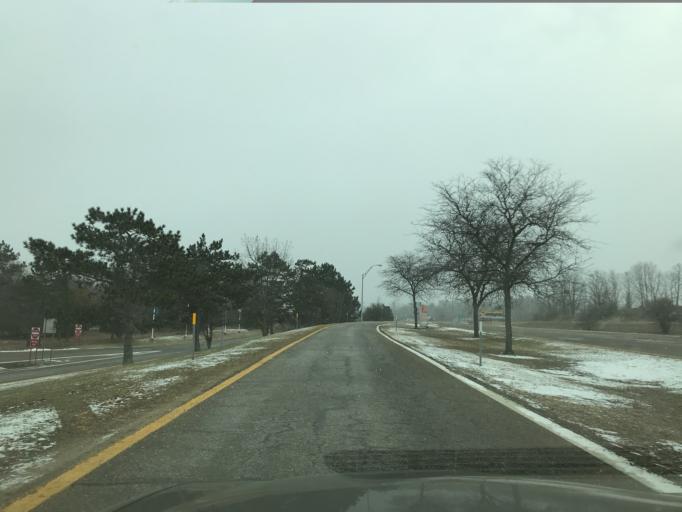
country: US
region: Michigan
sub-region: Clare County
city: Clare
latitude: 43.8496
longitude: -84.7761
